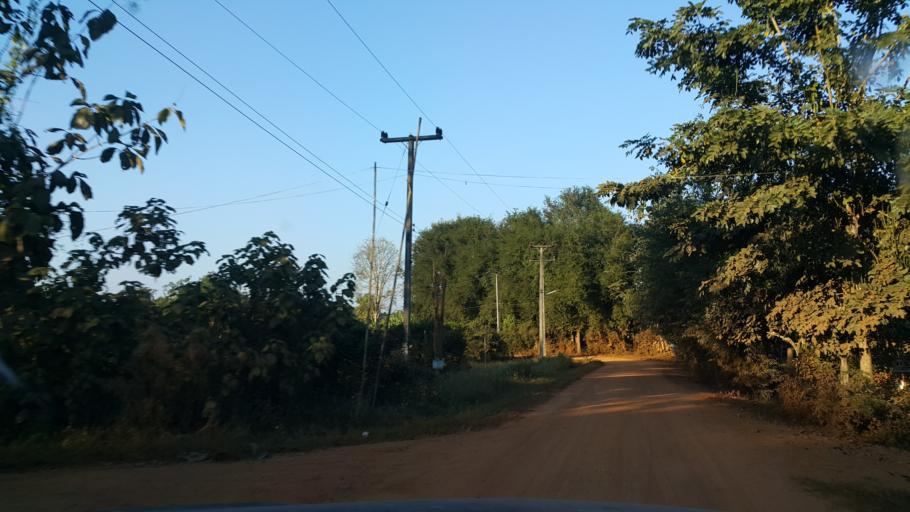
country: TH
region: Sukhothai
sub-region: Amphoe Si Satchanalai
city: Si Satchanalai
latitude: 17.6148
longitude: 99.6227
